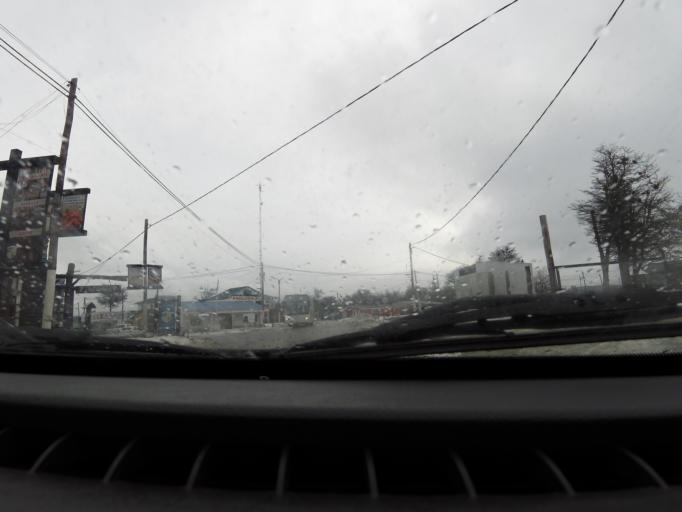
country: AR
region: Tierra del Fuego
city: Rio Grande
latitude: -54.5101
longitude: -67.1964
